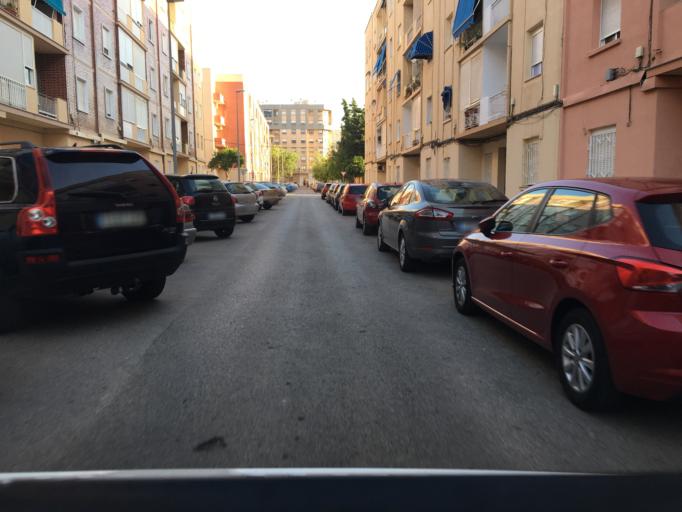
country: ES
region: Murcia
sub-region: Murcia
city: Cartagena
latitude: 37.6171
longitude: -0.9935
